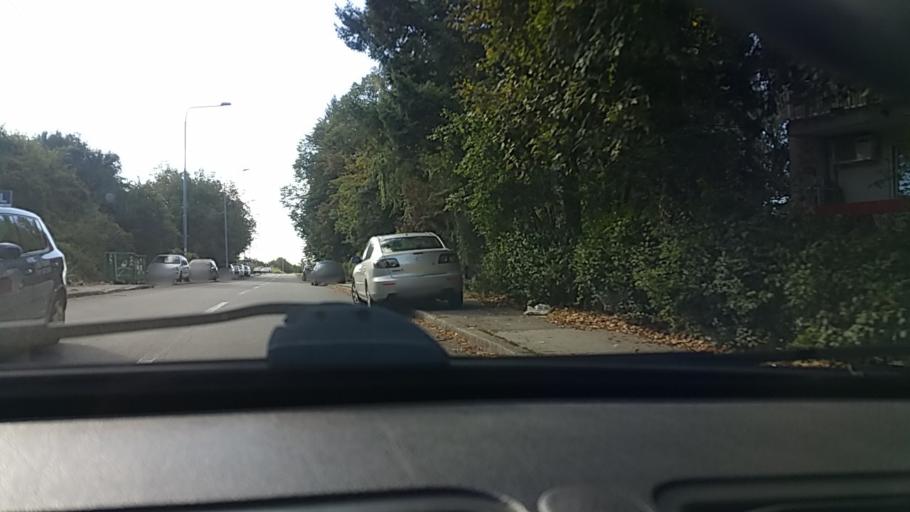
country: RS
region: Central Serbia
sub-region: Belgrade
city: Rakovica
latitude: 44.7473
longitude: 20.4612
